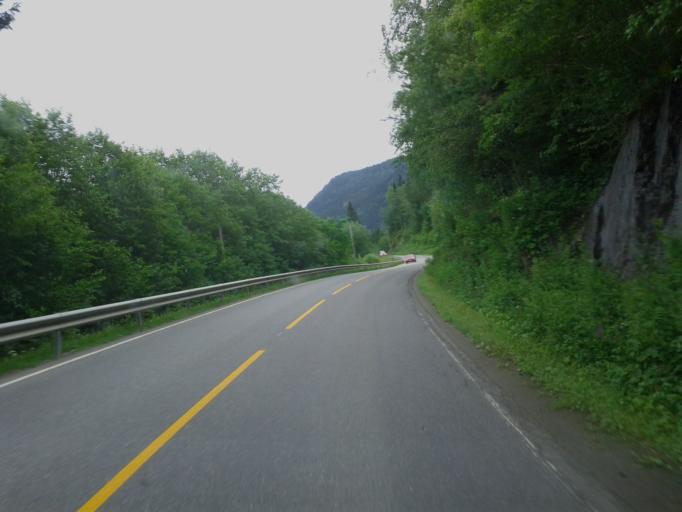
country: NO
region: Sor-Trondelag
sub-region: Midtre Gauldal
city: Storen
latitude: 63.0165
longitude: 10.3401
